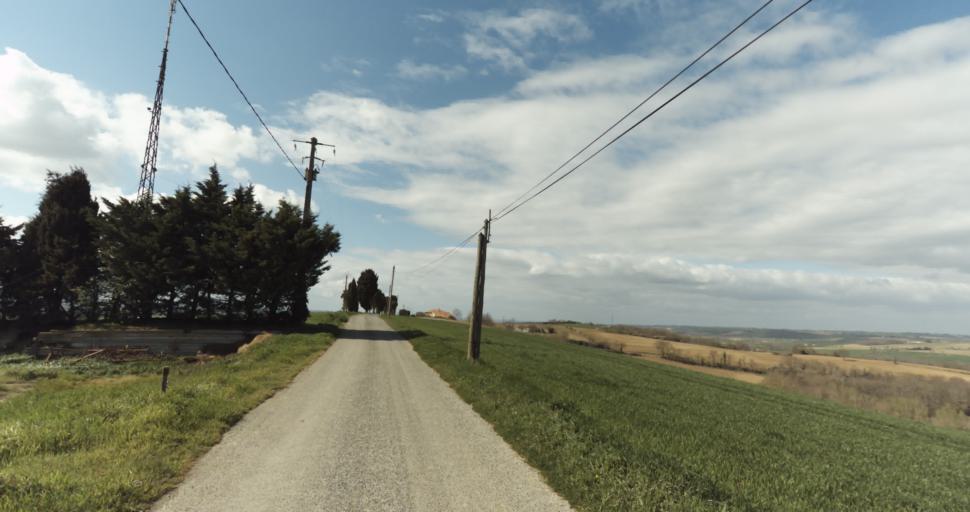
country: FR
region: Midi-Pyrenees
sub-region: Departement de la Haute-Garonne
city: Auterive
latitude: 43.3798
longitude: 1.4952
